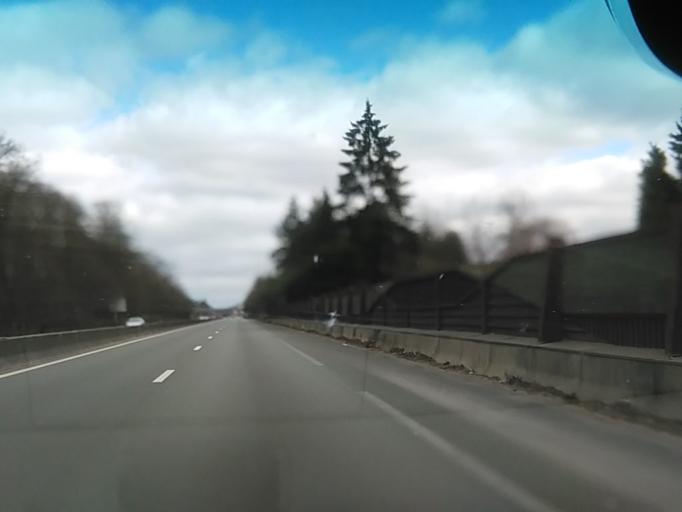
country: FR
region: Haute-Normandie
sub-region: Departement de la Seine-Maritime
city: Grand-Couronne
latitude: 49.3492
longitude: 1.0216
